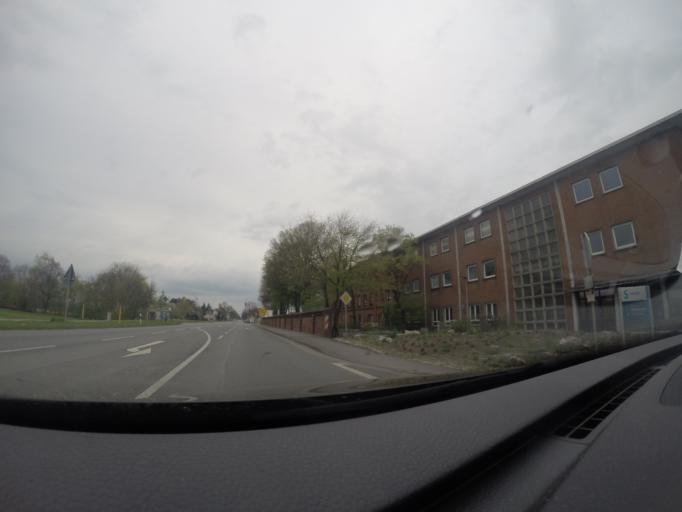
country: DE
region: North Rhine-Westphalia
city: Rheinberg
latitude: 51.5650
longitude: 6.5771
